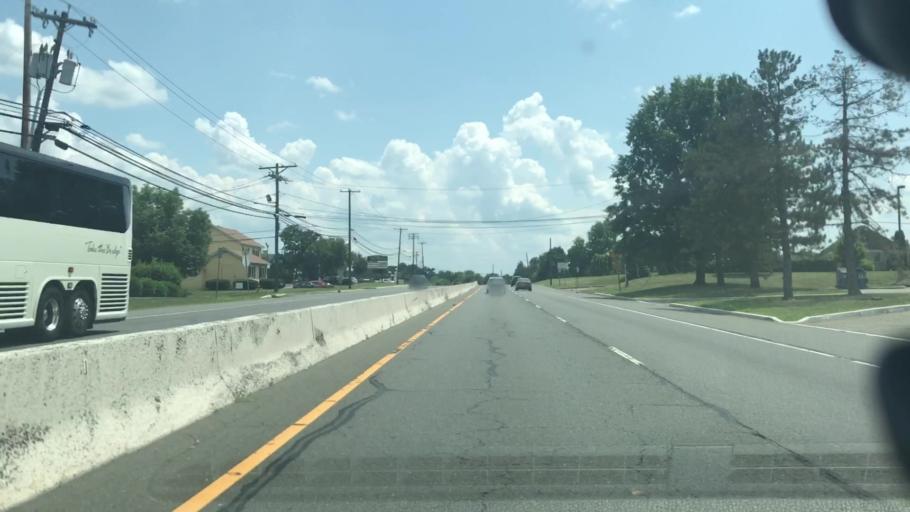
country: US
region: New Jersey
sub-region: Hunterdon County
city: Flemington
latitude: 40.4803
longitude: -74.8639
